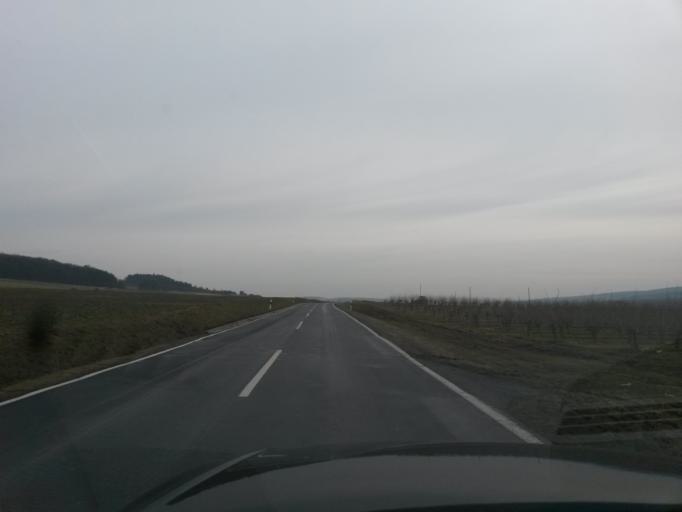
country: DE
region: Bavaria
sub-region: Regierungsbezirk Unterfranken
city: Sondheim vor der Rhoen
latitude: 50.4746
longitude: 10.1934
